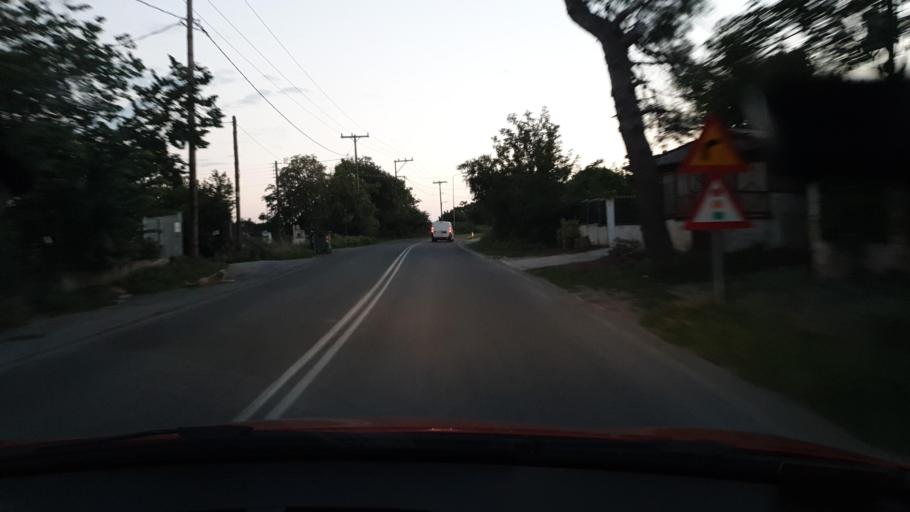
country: GR
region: Central Macedonia
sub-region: Nomos Thessalonikis
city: Agia Triada
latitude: 40.4945
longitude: 22.8719
